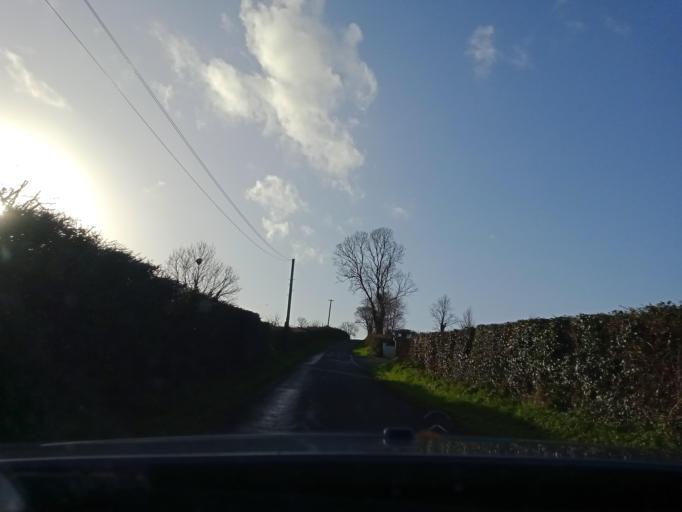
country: IE
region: Leinster
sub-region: Kilkenny
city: Callan
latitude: 52.4964
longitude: -7.3913
